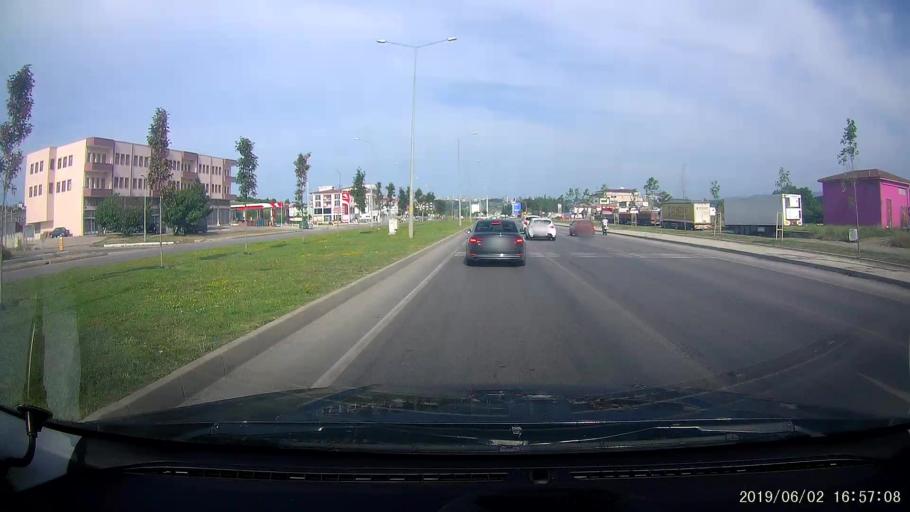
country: TR
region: Samsun
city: Samsun
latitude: 41.2912
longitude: 36.2716
